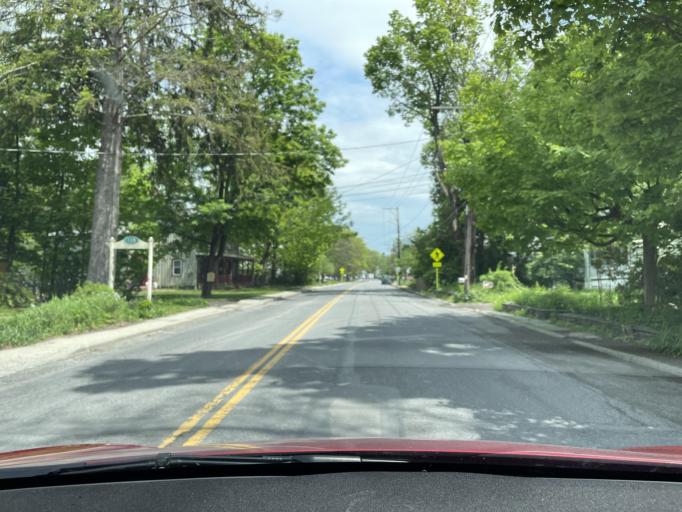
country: US
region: New York
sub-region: Ulster County
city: Woodstock
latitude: 42.0404
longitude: -74.1253
